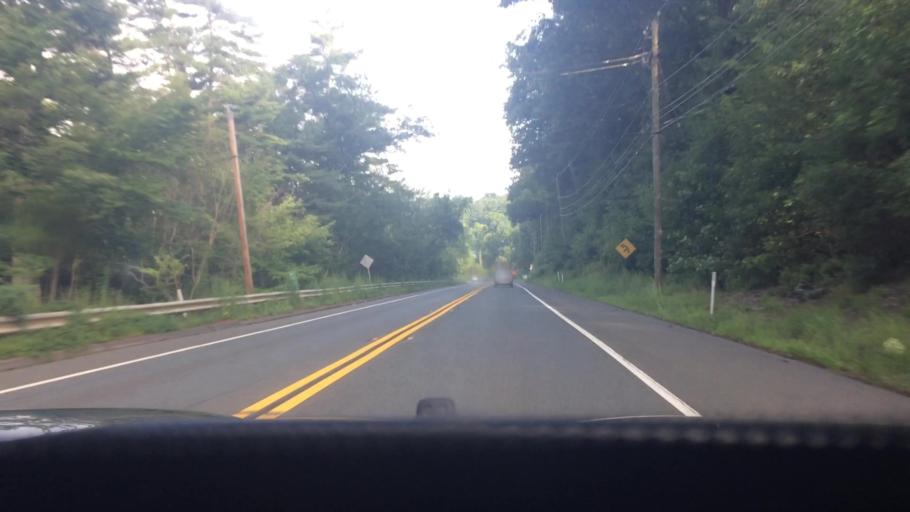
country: US
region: Massachusetts
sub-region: Franklin County
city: Turners Falls
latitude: 42.6069
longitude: -72.5305
